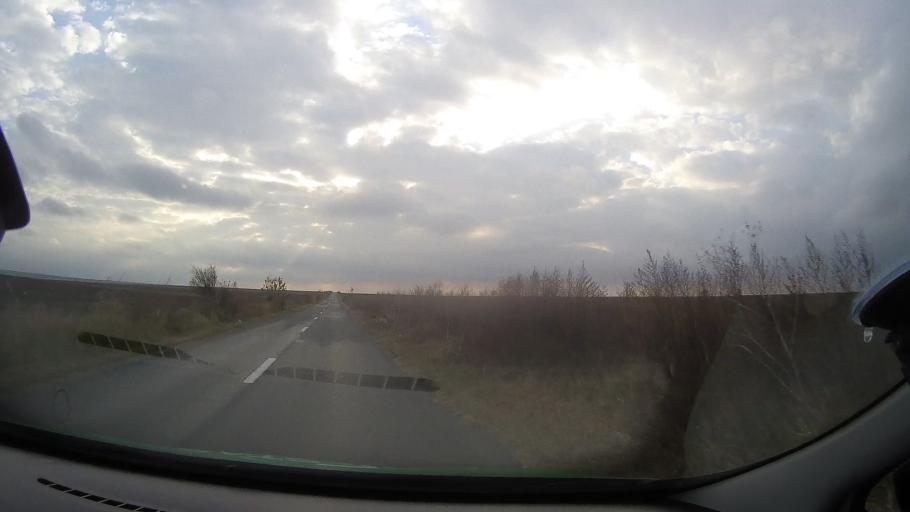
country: RO
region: Constanta
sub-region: Comuna Pestera
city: Pestera
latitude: 44.1302
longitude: 28.1147
